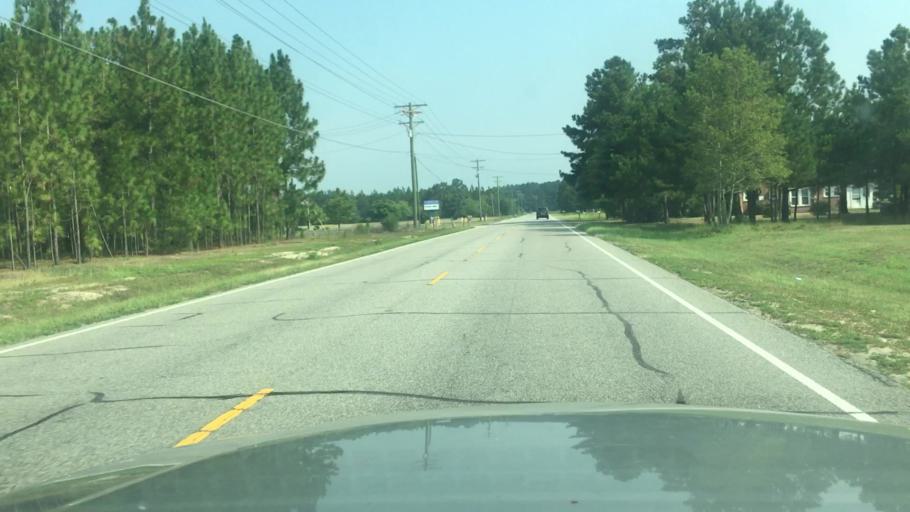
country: US
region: North Carolina
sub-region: Cumberland County
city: Hope Mills
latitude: 34.9070
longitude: -78.9034
